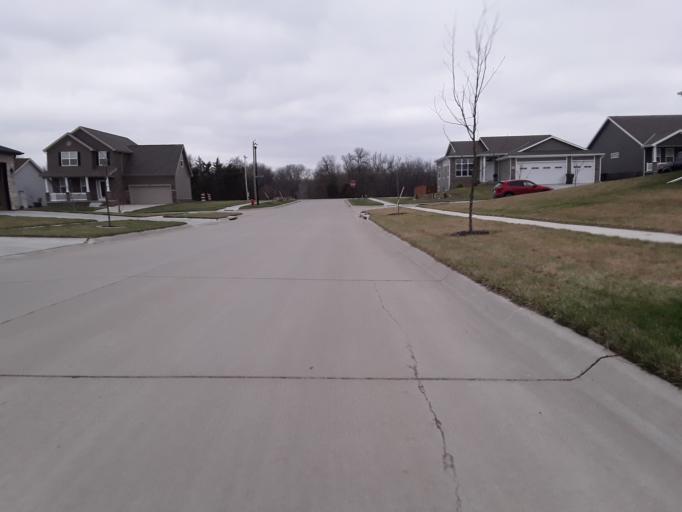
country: US
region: Nebraska
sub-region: Lancaster County
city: Lincoln
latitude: 40.8435
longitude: -96.5934
